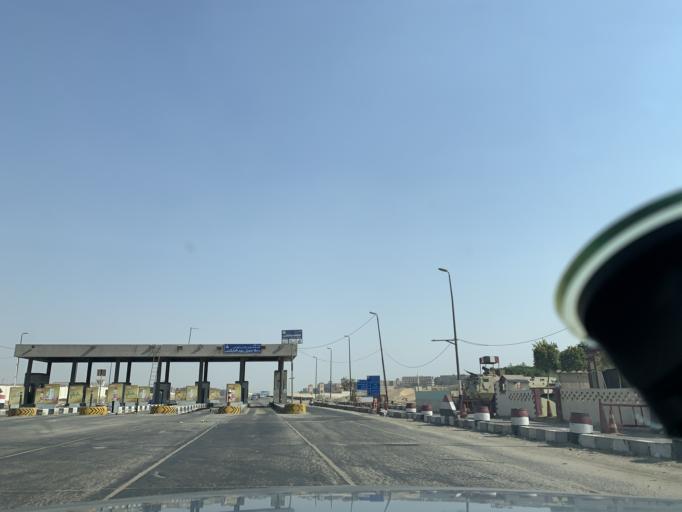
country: EG
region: Muhafazat al Qalyubiyah
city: Al Khankah
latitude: 30.1981
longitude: 31.4212
